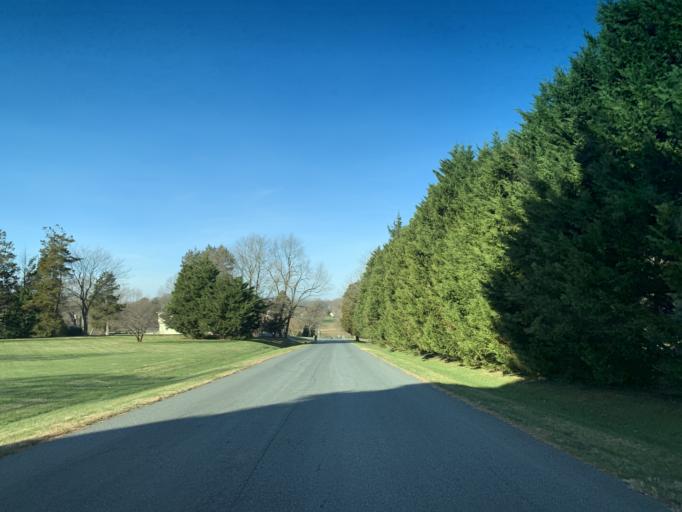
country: US
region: Maryland
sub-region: Harford County
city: South Bel Air
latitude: 39.5683
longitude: -76.2586
